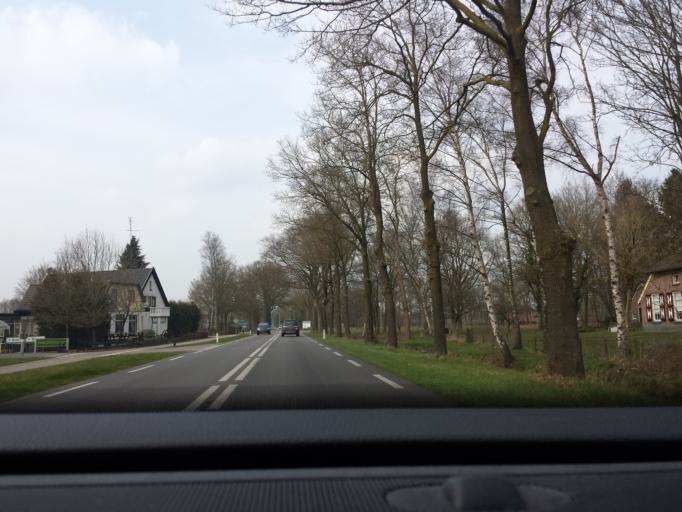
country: NL
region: Gelderland
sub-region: Gemeente Bronckhorst
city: Hengelo
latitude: 52.0918
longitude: 6.3139
